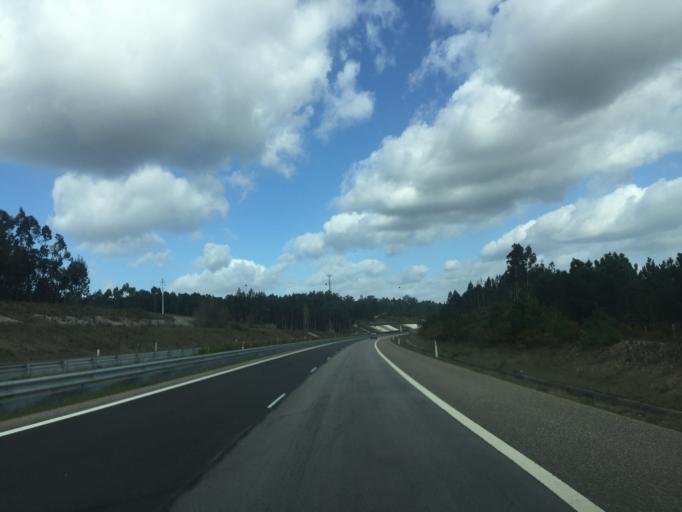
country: PT
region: Leiria
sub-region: Leiria
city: Amor
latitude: 39.7771
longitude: -8.8697
